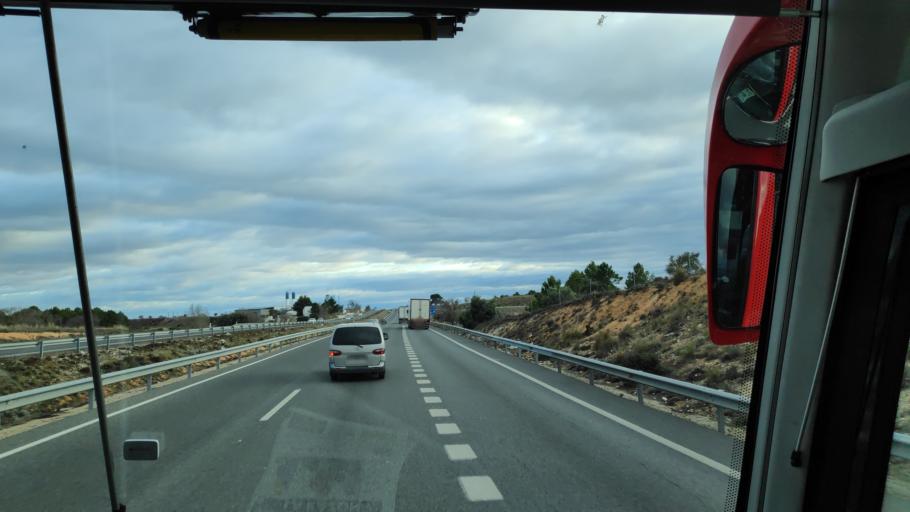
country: ES
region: Madrid
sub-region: Provincia de Madrid
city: Villarejo de Salvanes
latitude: 40.1883
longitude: -3.2987
